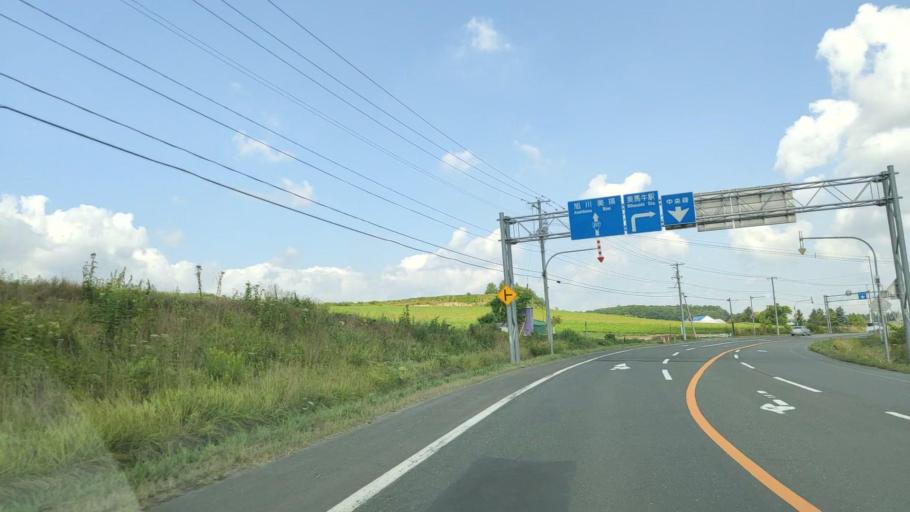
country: JP
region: Hokkaido
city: Shimo-furano
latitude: 43.5329
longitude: 142.4410
